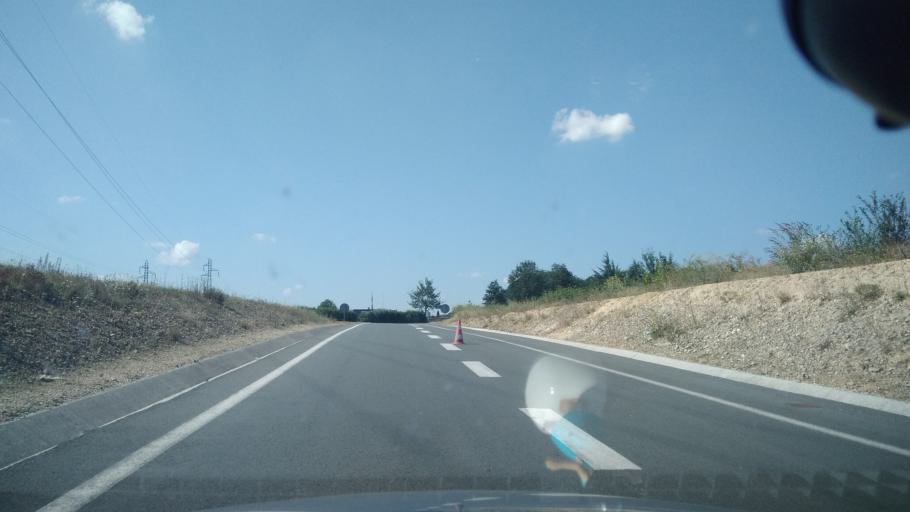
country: FR
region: Poitou-Charentes
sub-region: Departement de la Vienne
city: Migne-Auxances
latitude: 46.6210
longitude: 0.3499
